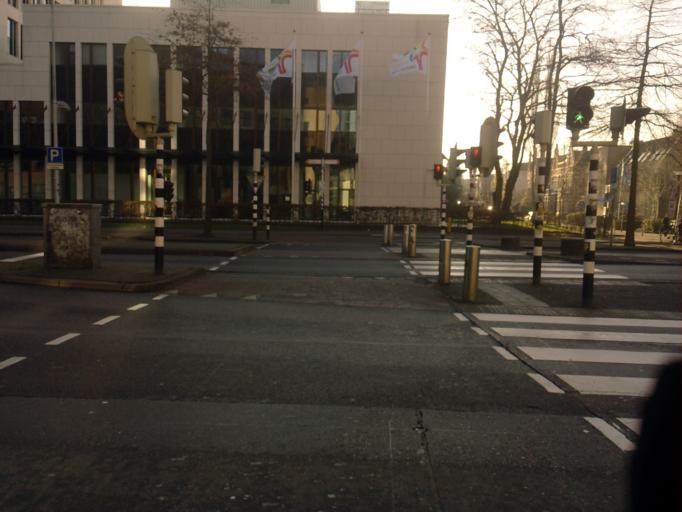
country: NL
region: Utrecht
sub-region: Gemeente Amersfoort
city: Amersfoort
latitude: 52.1527
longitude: 5.3760
